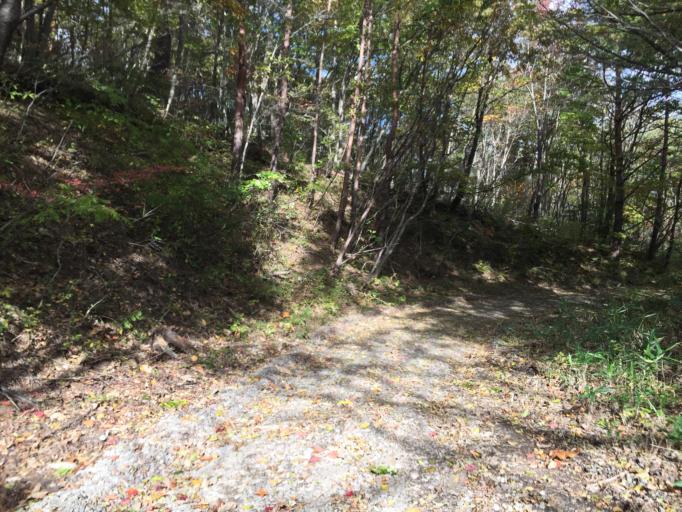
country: JP
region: Fukushima
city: Fukushima-shi
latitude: 37.6837
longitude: 140.3764
